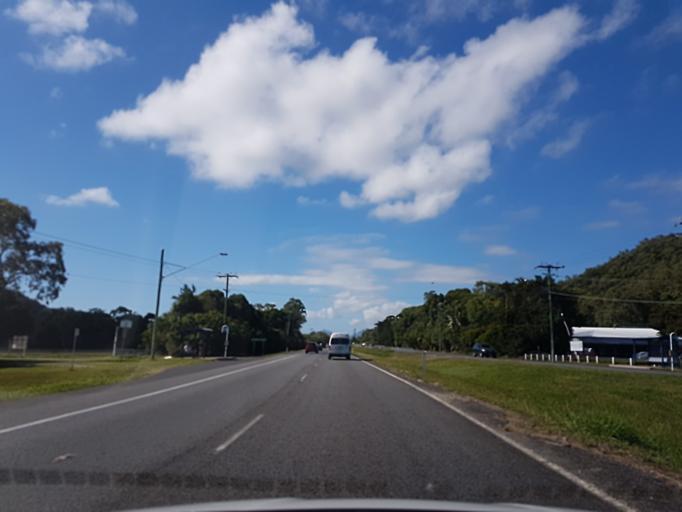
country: AU
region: Queensland
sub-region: Cairns
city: Trinity Beach
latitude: -16.7946
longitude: 145.6804
